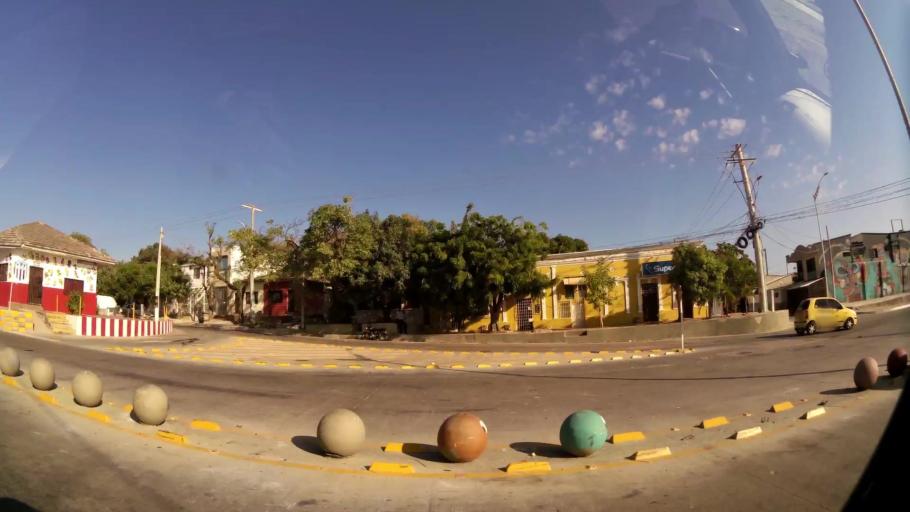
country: CO
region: Atlantico
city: Barranquilla
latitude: 10.9937
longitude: -74.7855
